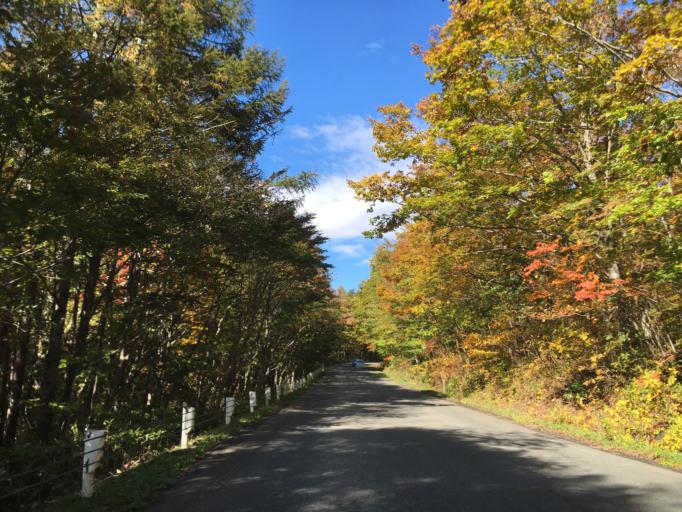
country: JP
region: Fukushima
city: Inawashiro
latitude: 37.5875
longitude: 140.2442
